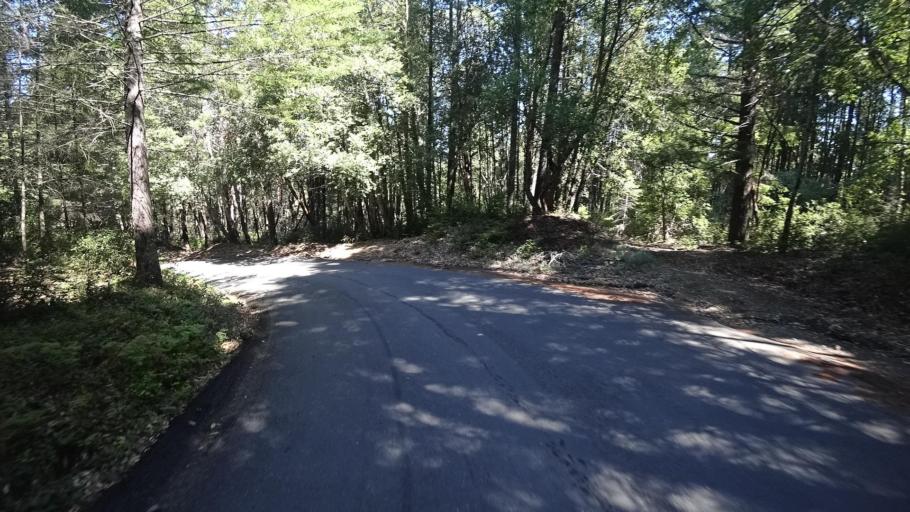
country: US
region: California
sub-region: Humboldt County
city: Redway
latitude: 40.1889
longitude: -124.0941
